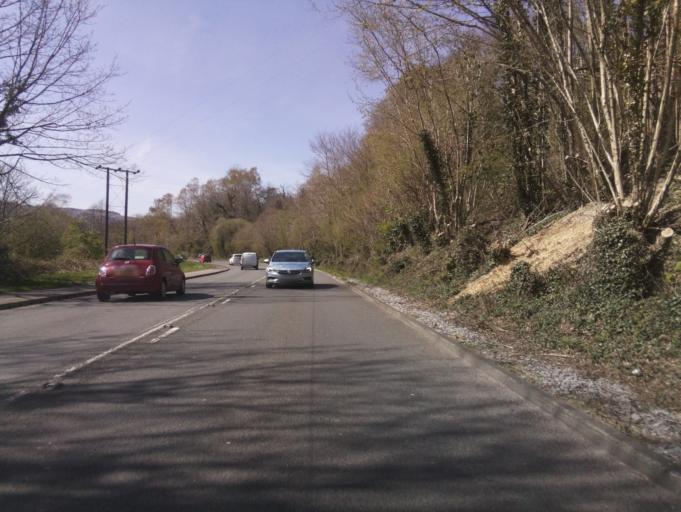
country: GB
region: Wales
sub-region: Merthyr Tydfil County Borough
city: Treharris
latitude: 51.6634
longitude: -3.3427
